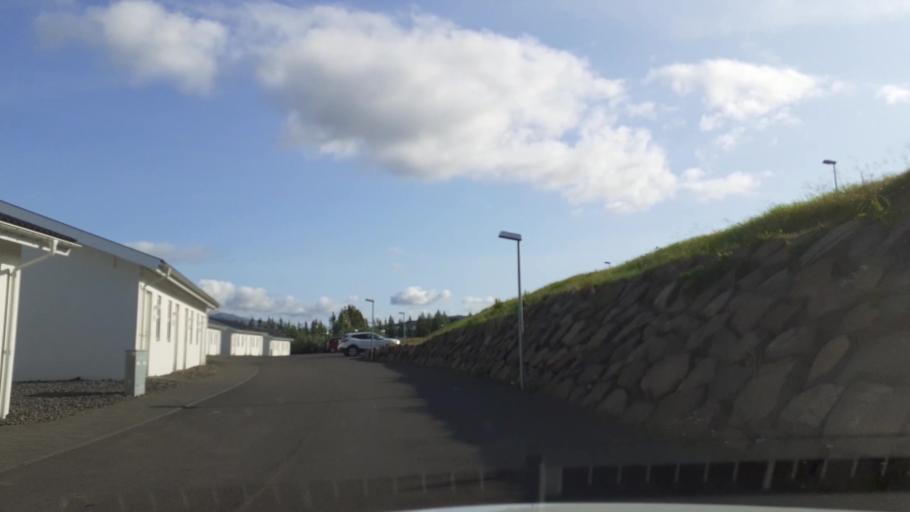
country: IS
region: Northeast
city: Akureyri
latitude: 65.6703
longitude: -18.0950
